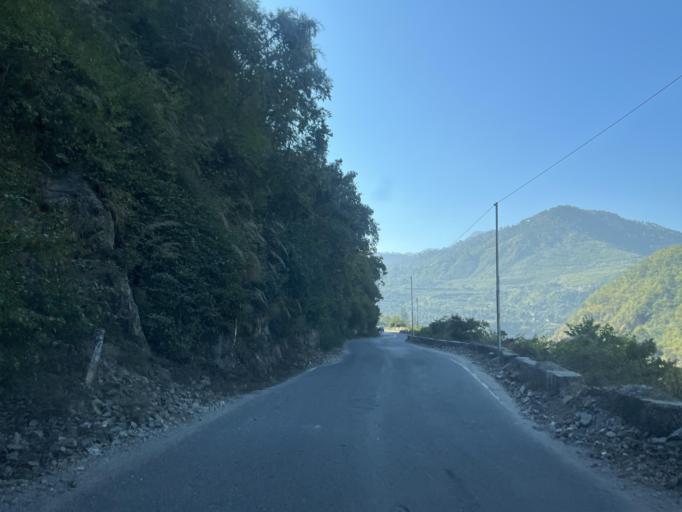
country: IN
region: Uttarakhand
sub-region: Naini Tal
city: Naini Tal
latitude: 29.5166
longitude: 79.4799
